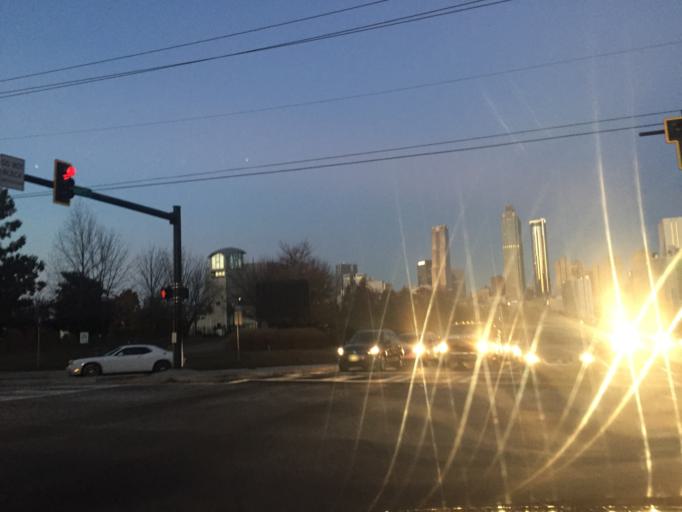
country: US
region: Georgia
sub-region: Fulton County
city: Atlanta
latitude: 33.7602
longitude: -84.3720
